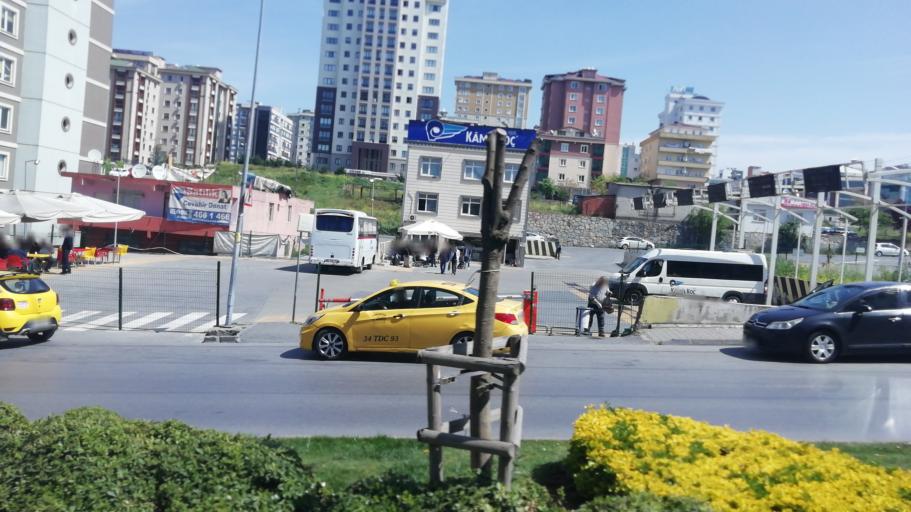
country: TR
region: Istanbul
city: Umraniye
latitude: 41.0002
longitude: 29.1463
